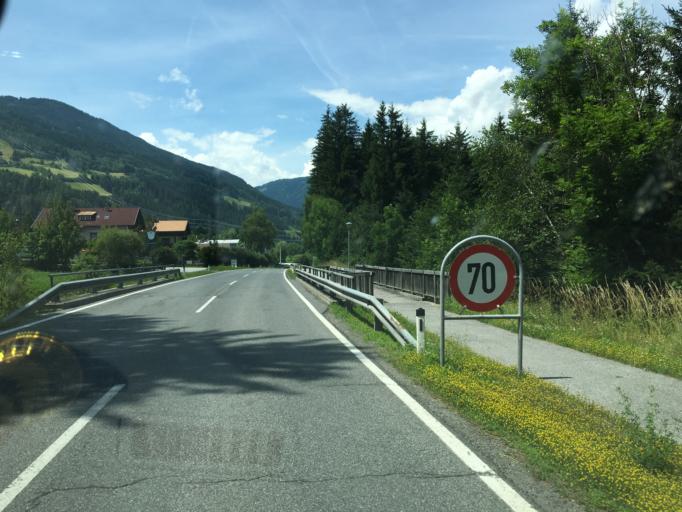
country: AT
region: Carinthia
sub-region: Politischer Bezirk Spittal an der Drau
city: Rangersdorf
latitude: 46.8540
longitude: 12.9280
